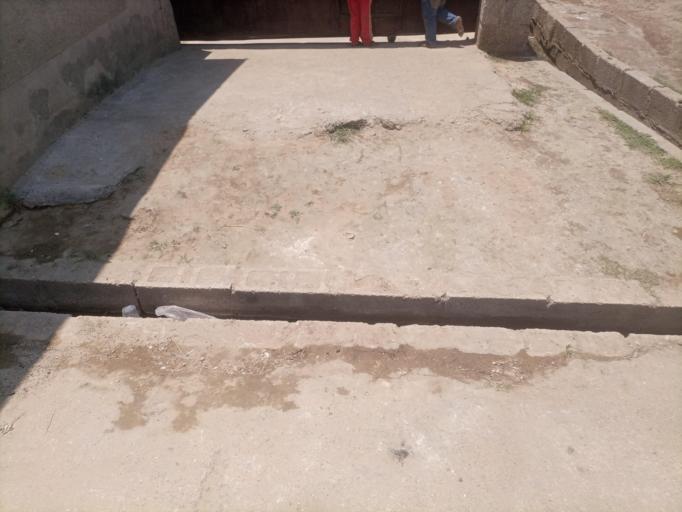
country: ZM
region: Lusaka
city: Lusaka
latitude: -15.4083
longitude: 28.3774
